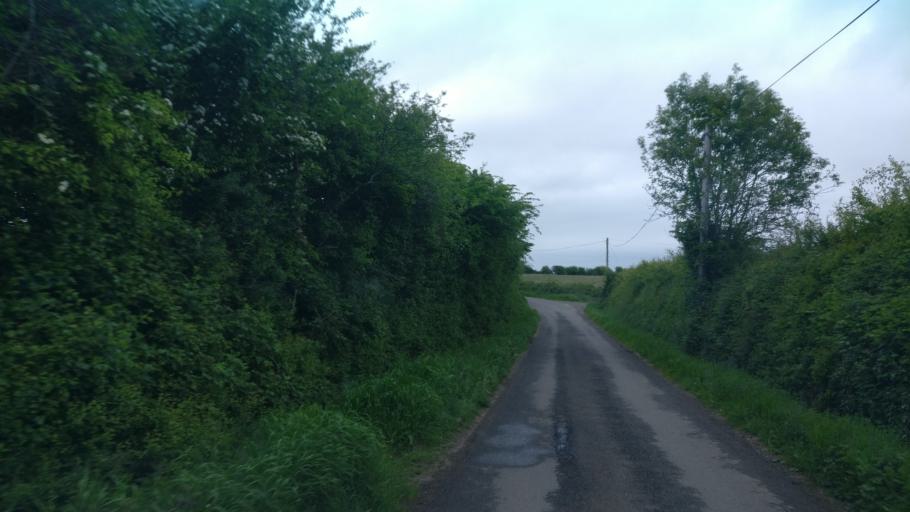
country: IE
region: Connaught
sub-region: County Galway
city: Portumna
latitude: 53.1344
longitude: -8.2920
